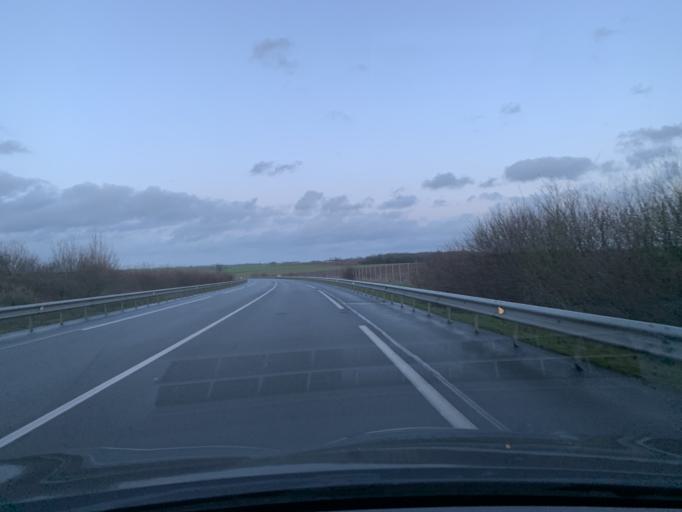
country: FR
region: Nord-Pas-de-Calais
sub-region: Departement du Nord
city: Escaudoeuvres
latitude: 50.1501
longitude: 3.2846
